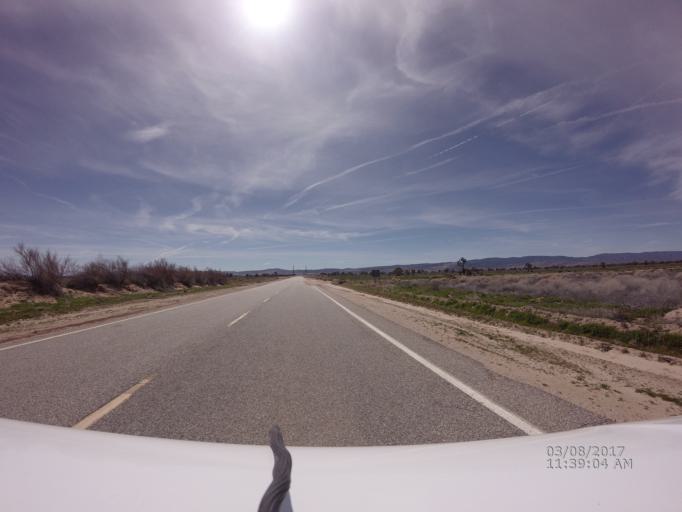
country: US
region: California
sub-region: Los Angeles County
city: Green Valley
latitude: 34.8047
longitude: -118.4315
